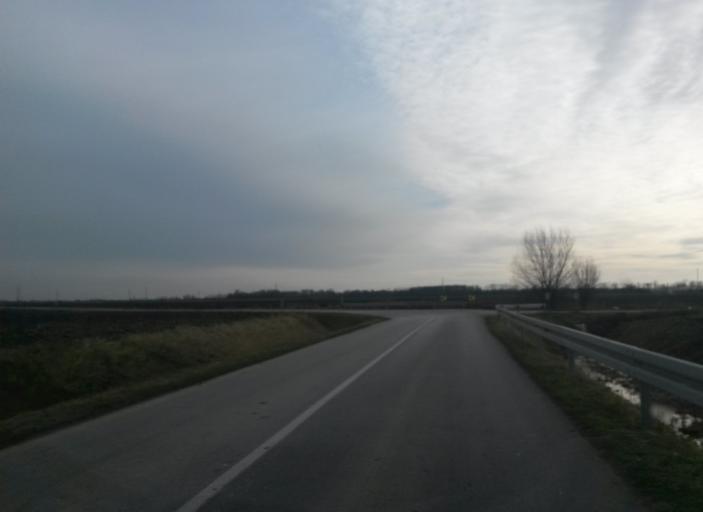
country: HR
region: Osjecko-Baranjska
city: Ovcara
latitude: 45.5031
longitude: 18.5981
